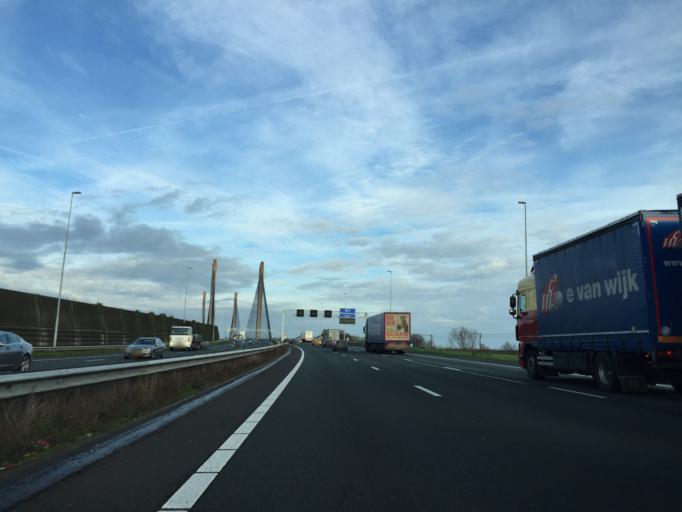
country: NL
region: Gelderland
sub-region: Gemeente Zaltbommel
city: Zaltbommel
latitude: 51.8129
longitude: 5.2606
